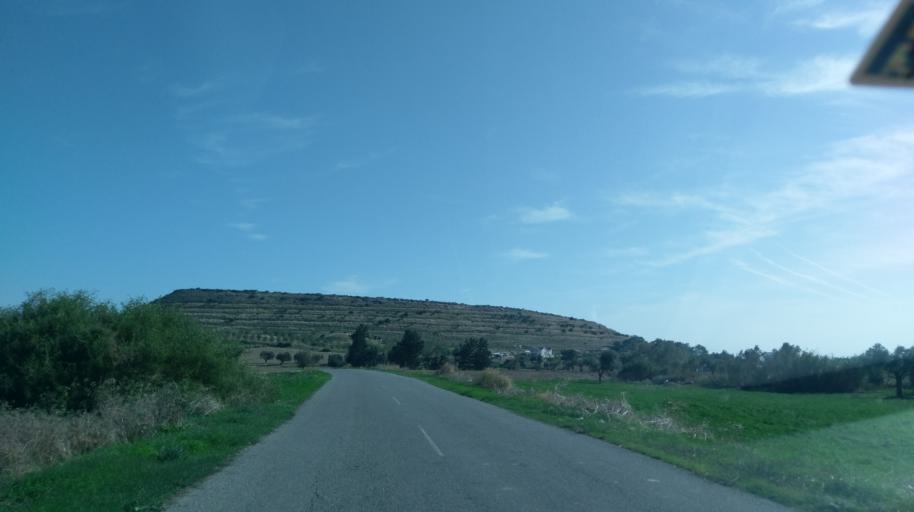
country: CY
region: Ammochostos
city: Trikomo
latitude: 35.3318
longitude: 33.9305
